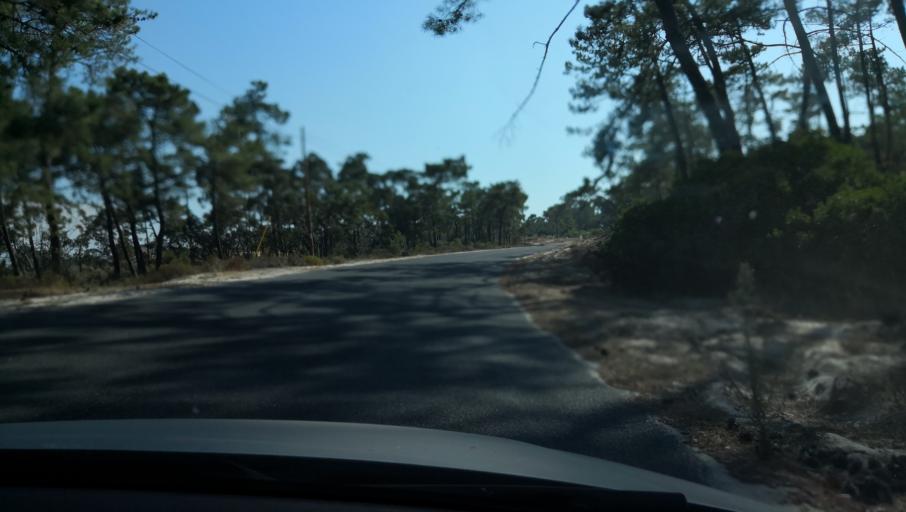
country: PT
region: Setubal
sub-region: Setubal
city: Setubal
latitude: 38.4672
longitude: -8.8695
